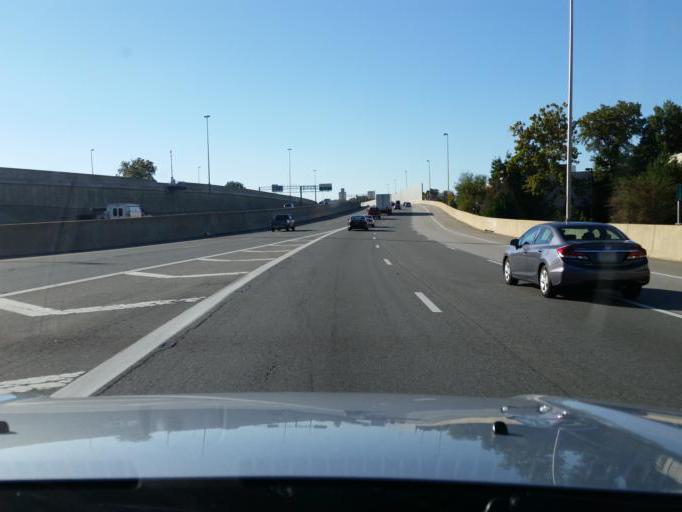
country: US
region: Virginia
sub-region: Fairfax County
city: Springfield
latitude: 38.7938
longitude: -77.1815
